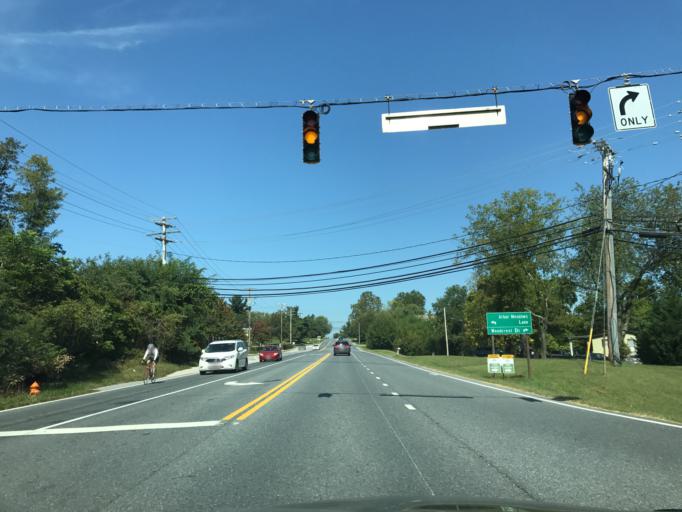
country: US
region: Maryland
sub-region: Anne Arundel County
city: Jessup
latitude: 39.1968
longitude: -76.7942
